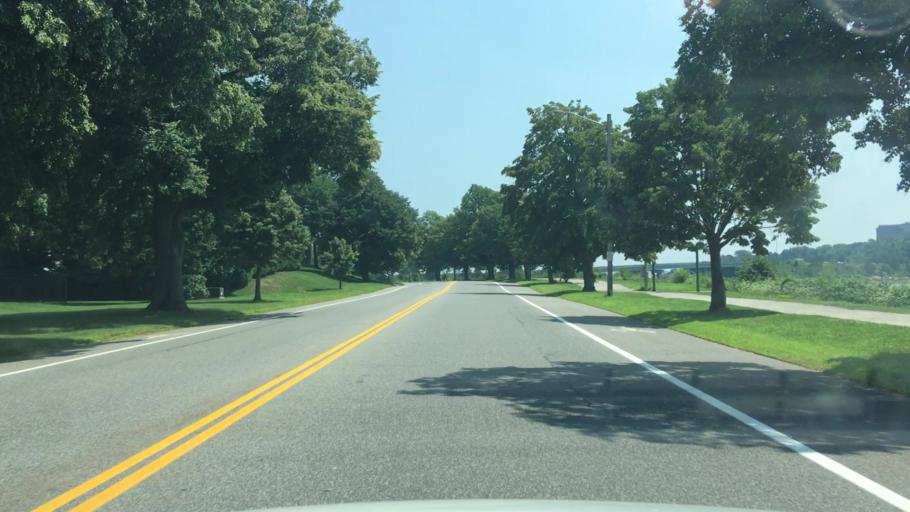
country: US
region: Maine
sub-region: Cumberland County
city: Portland
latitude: 43.6791
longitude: -70.2630
